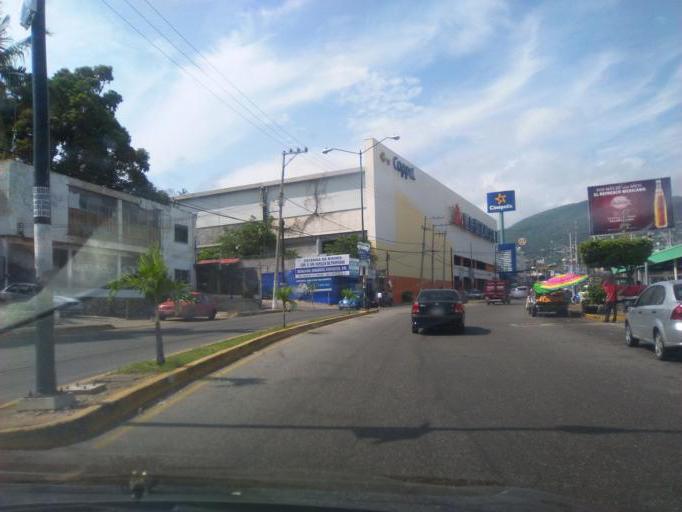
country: MX
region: Guerrero
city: Acapulco de Juarez
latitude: 16.8571
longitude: -99.9146
